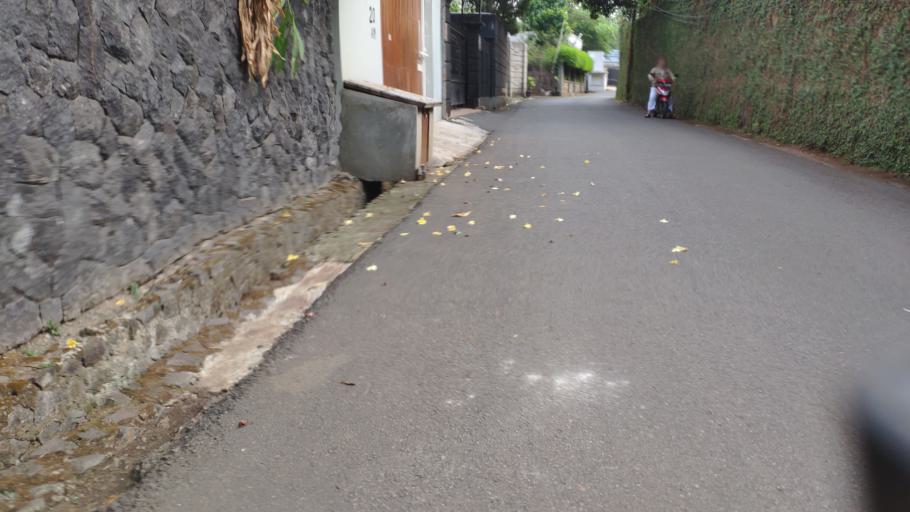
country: ID
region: West Java
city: Pamulang
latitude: -6.3109
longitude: 106.8069
